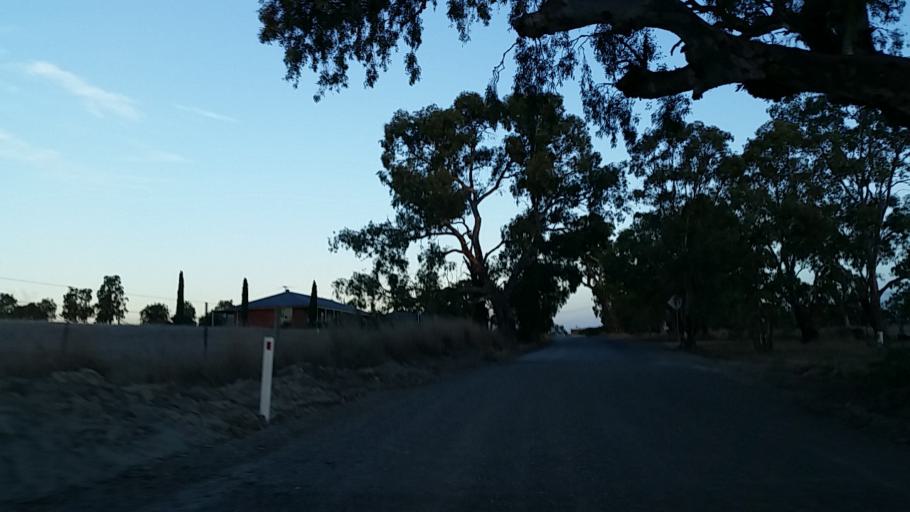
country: AU
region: South Australia
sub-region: Mount Barker
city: Nairne
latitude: -35.0827
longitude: 138.9346
